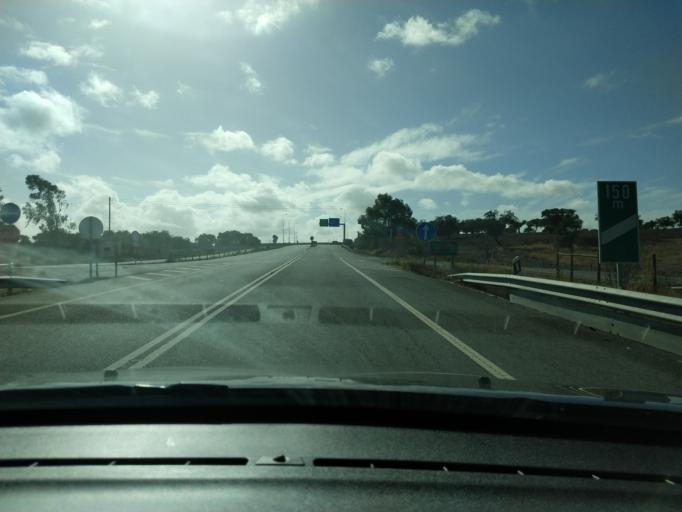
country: PT
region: Beja
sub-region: Castro Verde
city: Castro Verde
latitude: 37.6732
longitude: -8.1482
